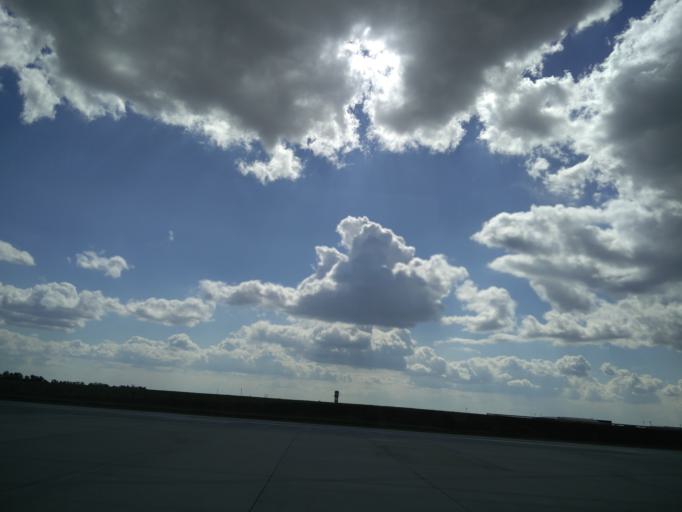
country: HU
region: Pest
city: Vecses
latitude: 47.4328
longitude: 19.2565
